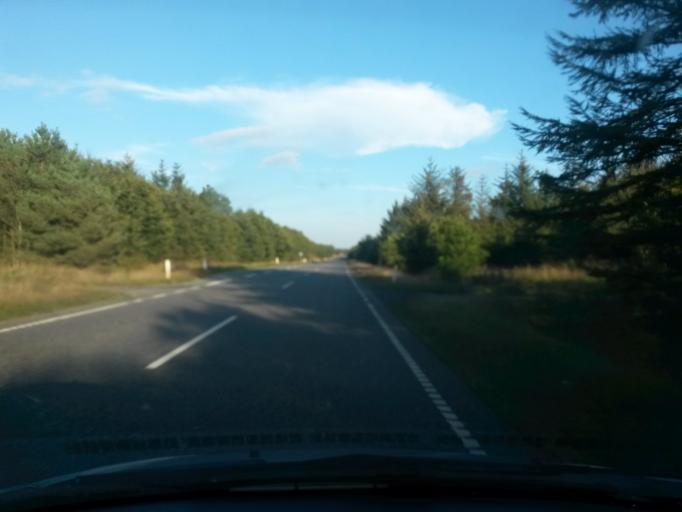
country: DK
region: Central Jutland
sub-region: Herning Kommune
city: Sunds
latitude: 56.3319
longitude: 8.9738
